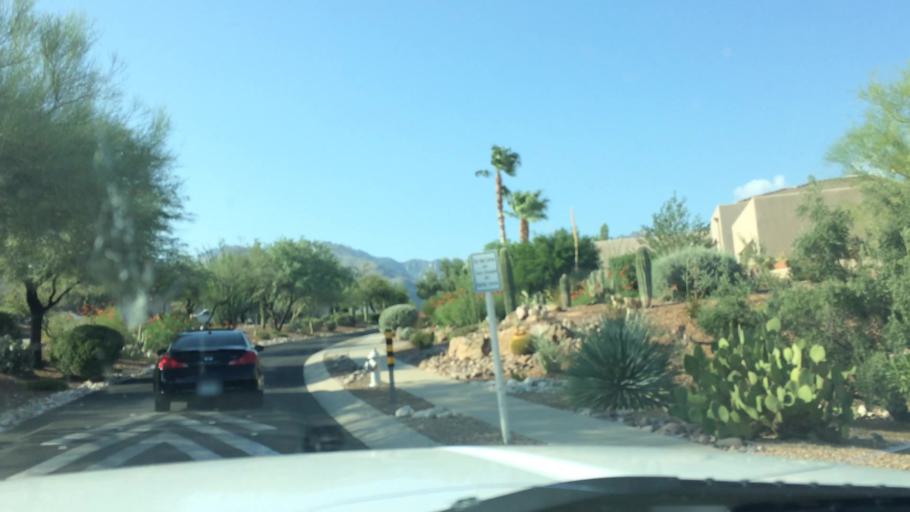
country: US
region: Arizona
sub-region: Pima County
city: Catalina Foothills
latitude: 32.2962
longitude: -110.8326
